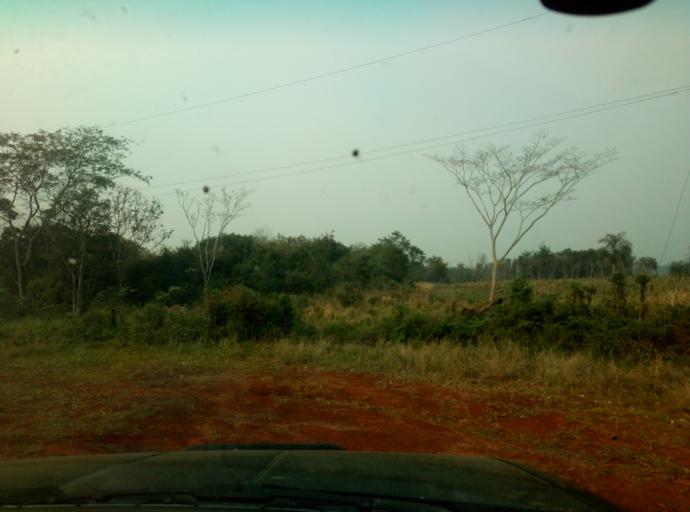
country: PY
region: Caaguazu
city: Carayao
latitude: -25.2102
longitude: -56.2241
